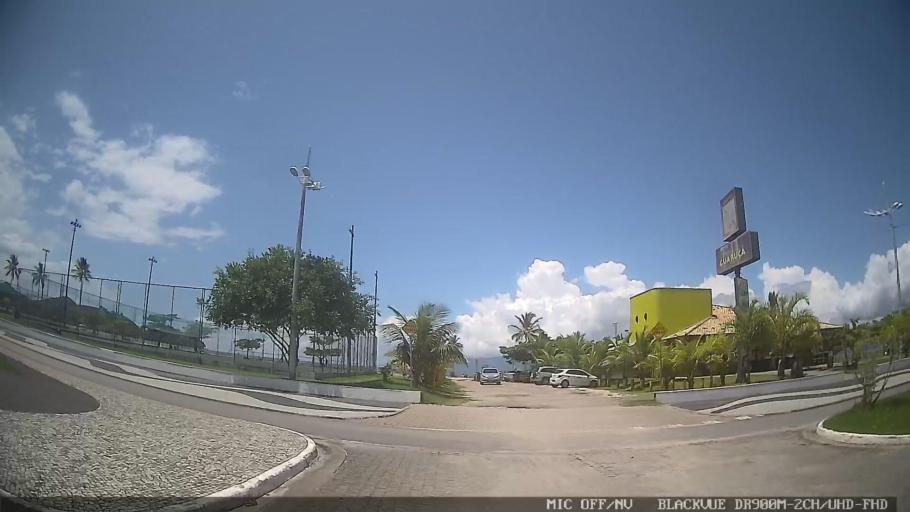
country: BR
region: Sao Paulo
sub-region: Caraguatatuba
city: Caraguatatuba
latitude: -23.6286
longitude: -45.4147
